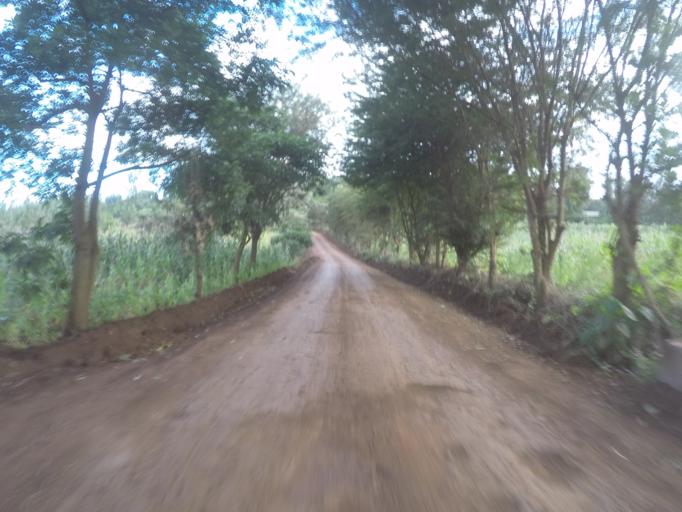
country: TZ
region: Arusha
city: Kiratu
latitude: -3.3214
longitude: 35.6634
